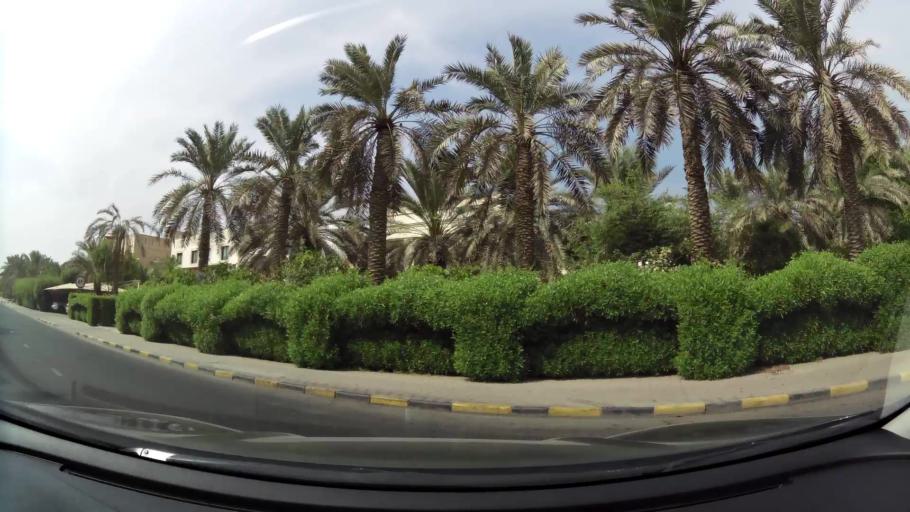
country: KW
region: Al Asimah
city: Ad Dasmah
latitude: 29.3562
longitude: 47.9893
